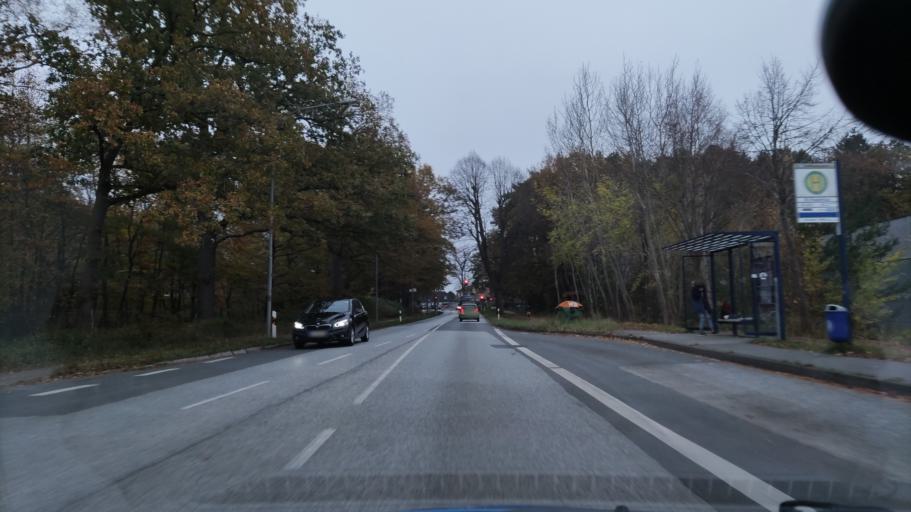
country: DE
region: Schleswig-Holstein
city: Gross Gronau
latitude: 53.8247
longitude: 10.7213
